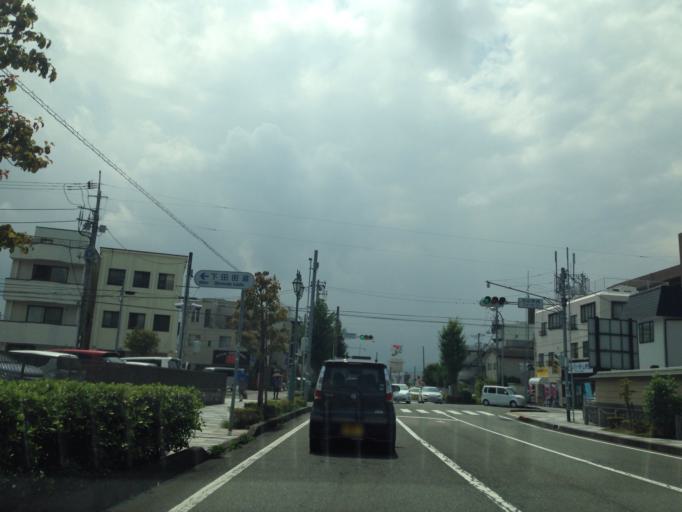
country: JP
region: Shizuoka
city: Mishima
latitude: 35.1178
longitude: 138.9194
